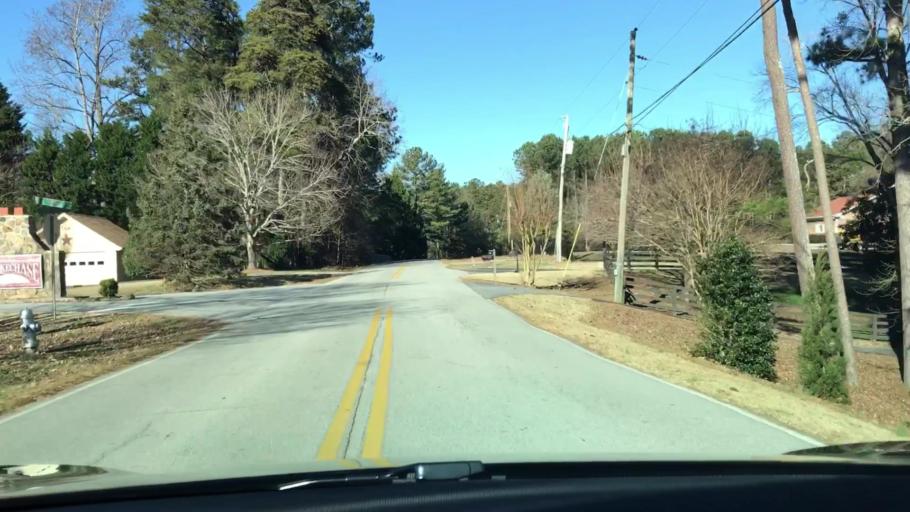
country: US
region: Georgia
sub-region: Gwinnett County
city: Buford
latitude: 34.1541
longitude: -84.0084
